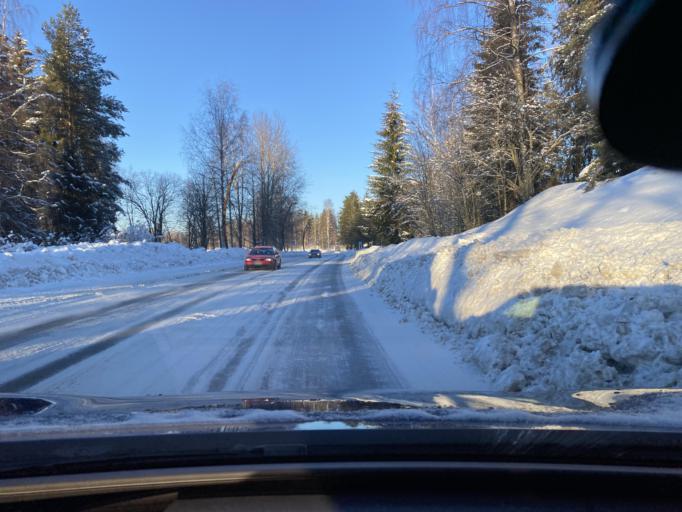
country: FI
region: Southern Savonia
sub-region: Mikkeli
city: Kangasniemi
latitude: 61.9927
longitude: 26.6452
